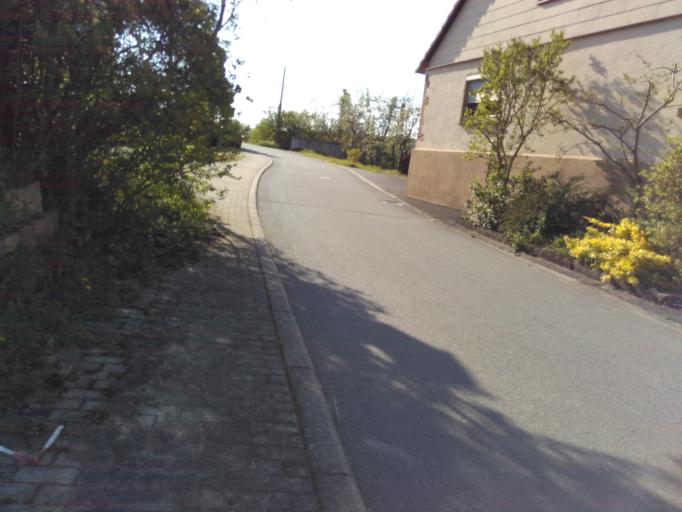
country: DE
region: Baden-Wuerttemberg
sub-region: Karlsruhe Region
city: Rosenberg
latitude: 49.4727
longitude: 9.5024
